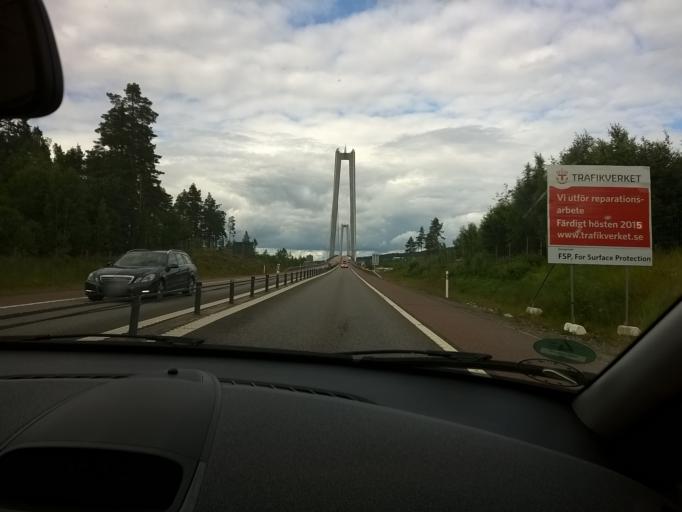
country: SE
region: Vaesternorrland
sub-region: Haernoesands Kommun
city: Haernoesand
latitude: 62.7889
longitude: 17.9237
